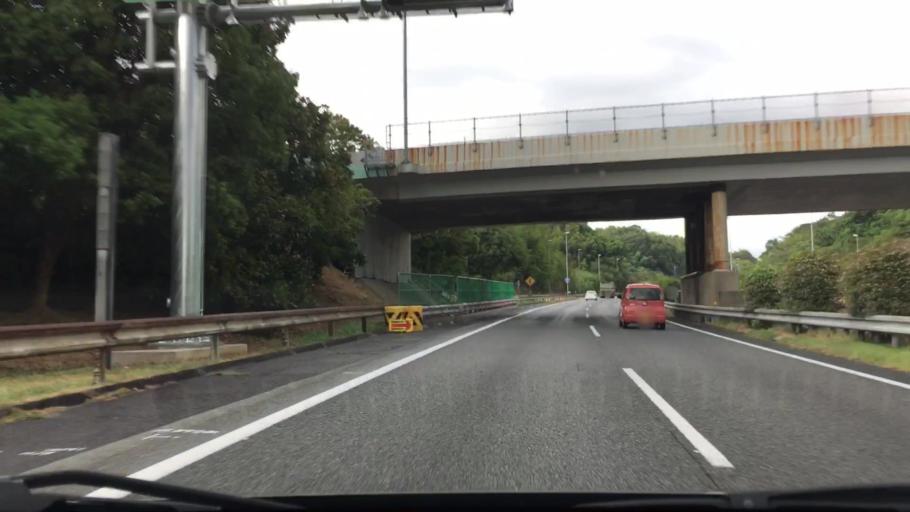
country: JP
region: Fukuoka
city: Koga
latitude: 33.7185
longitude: 130.4930
